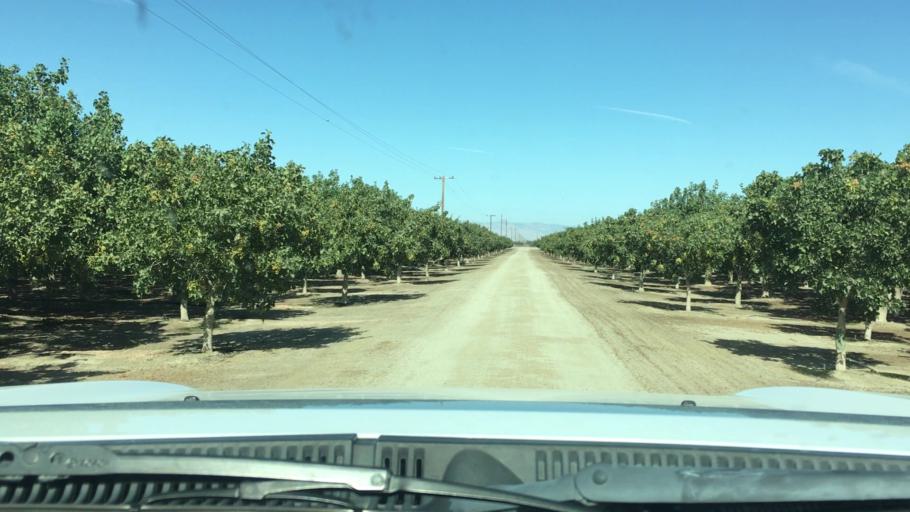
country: US
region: California
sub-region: Kern County
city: Buttonwillow
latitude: 35.3694
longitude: -119.3950
